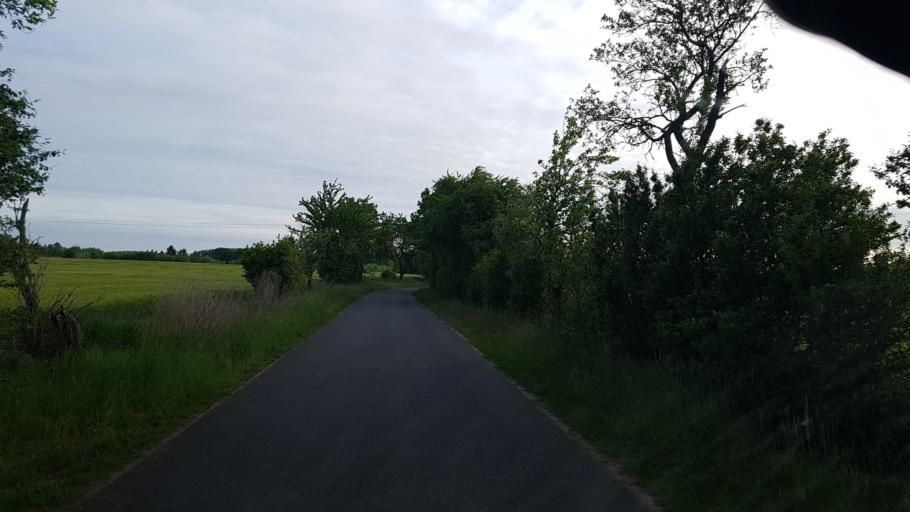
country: DE
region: Brandenburg
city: Luckau
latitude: 51.8154
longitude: 13.6421
